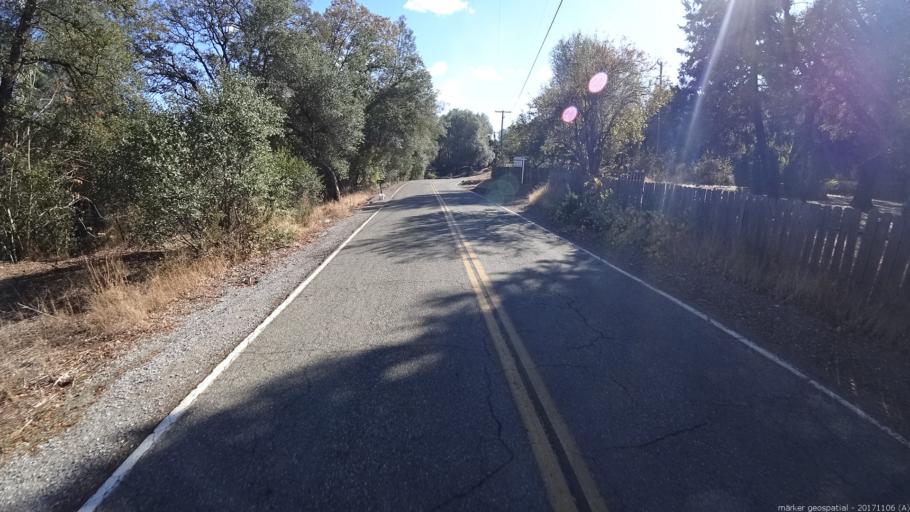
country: US
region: California
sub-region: Shasta County
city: Palo Cedro
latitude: 40.5799
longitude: -122.3009
